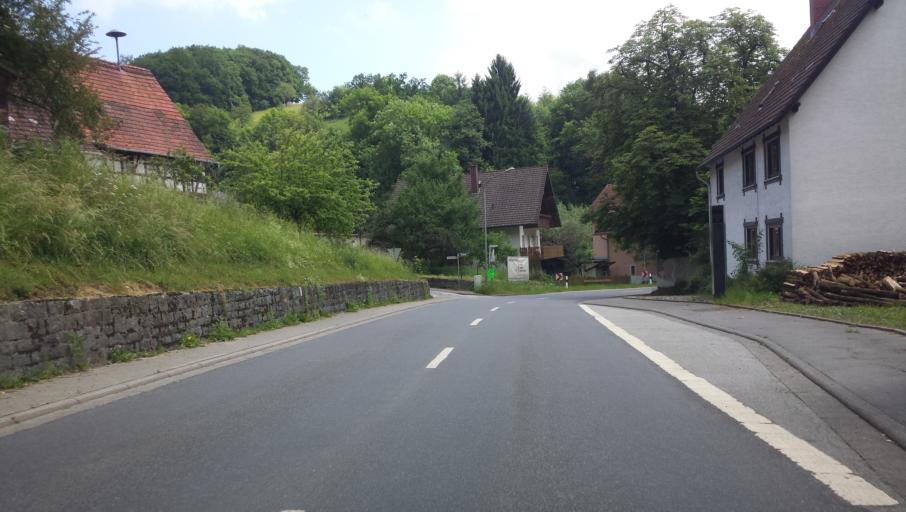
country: DE
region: Hesse
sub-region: Regierungsbezirk Darmstadt
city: Lindenfels
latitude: 49.6917
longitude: 8.7602
